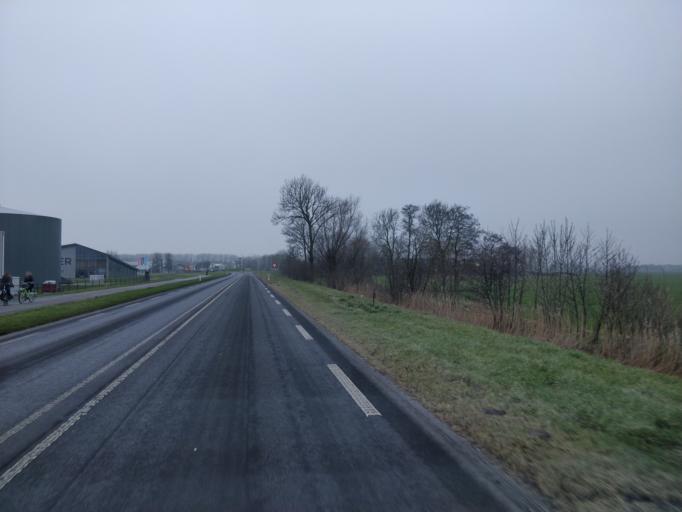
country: NL
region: Friesland
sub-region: Menameradiel
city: Berltsum
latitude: 53.2401
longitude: 5.6719
